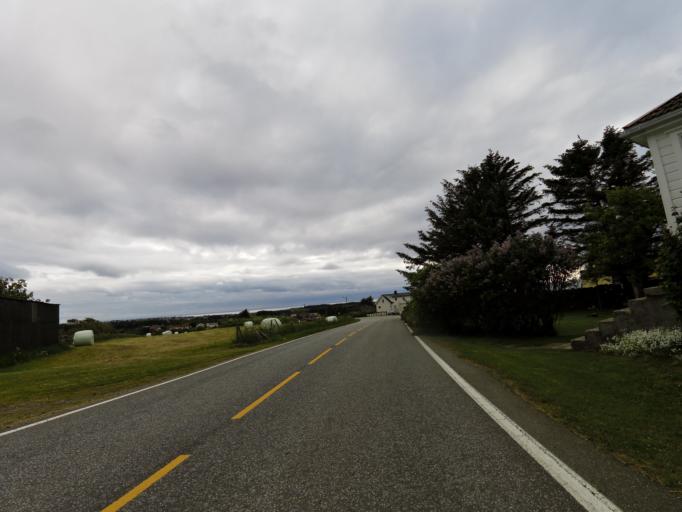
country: NO
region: Vest-Agder
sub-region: Farsund
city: Vestbygd
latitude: 58.1248
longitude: 6.6072
